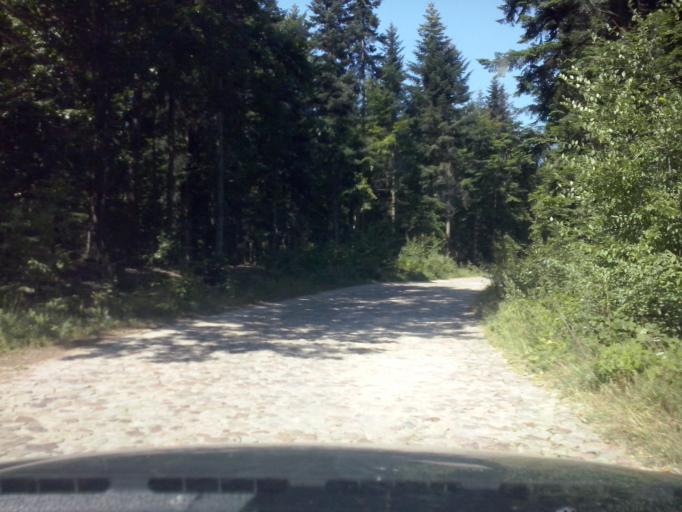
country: PL
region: Swietokrzyskie
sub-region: Powiat kielecki
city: Bieliny
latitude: 50.7812
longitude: 20.9306
